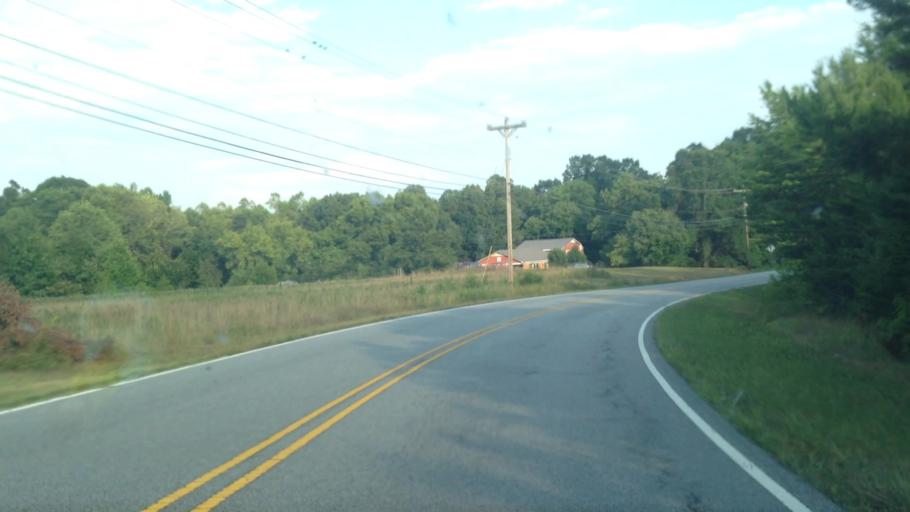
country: US
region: North Carolina
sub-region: Davidson County
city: Wallburg
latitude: 35.9693
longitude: -80.0845
